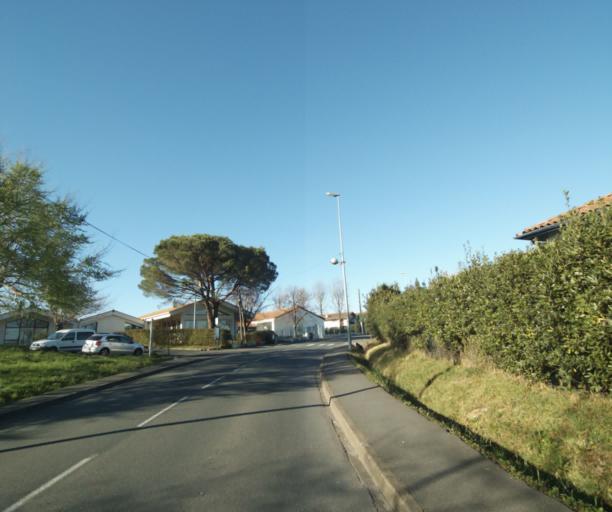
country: FR
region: Aquitaine
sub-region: Departement des Pyrenees-Atlantiques
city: Hendaye
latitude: 43.3667
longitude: -1.7568
